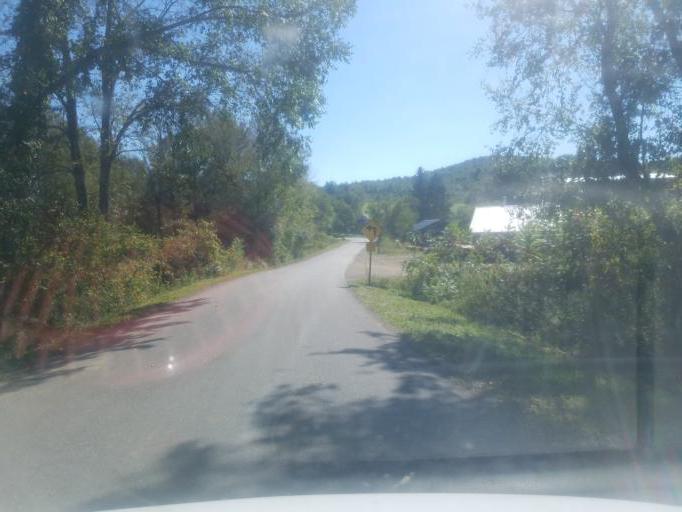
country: US
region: New York
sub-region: Allegany County
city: Cuba
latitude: 42.3033
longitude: -78.1994
